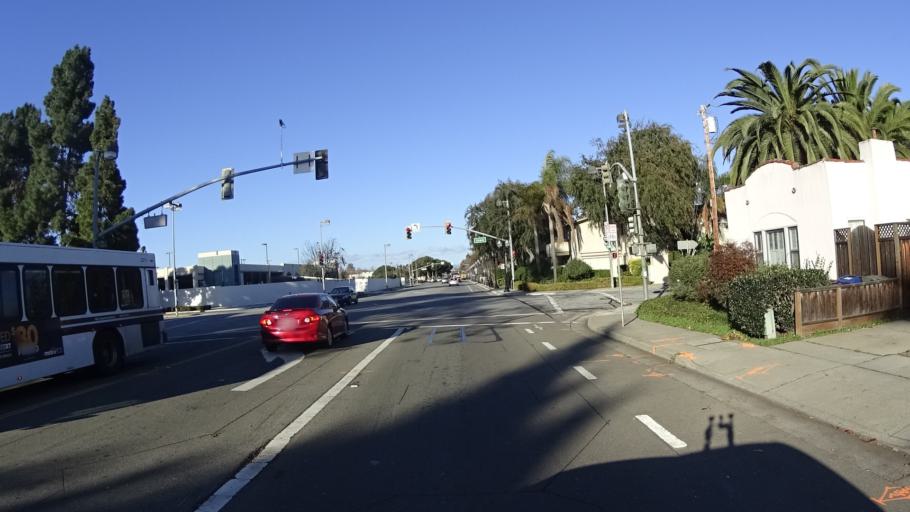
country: US
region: California
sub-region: Santa Clara County
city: Sunnyvale
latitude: 37.3722
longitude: -122.0305
